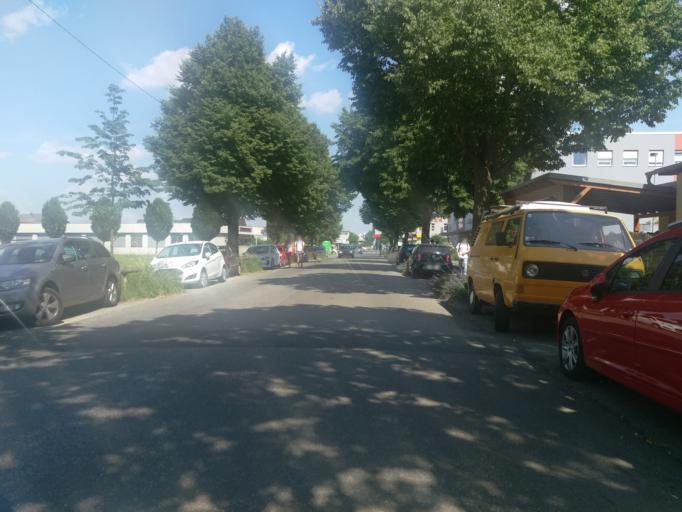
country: AT
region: Styria
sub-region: Politischer Bezirk Graz-Umgebung
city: Seiersberg
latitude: 47.0254
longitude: 15.3991
